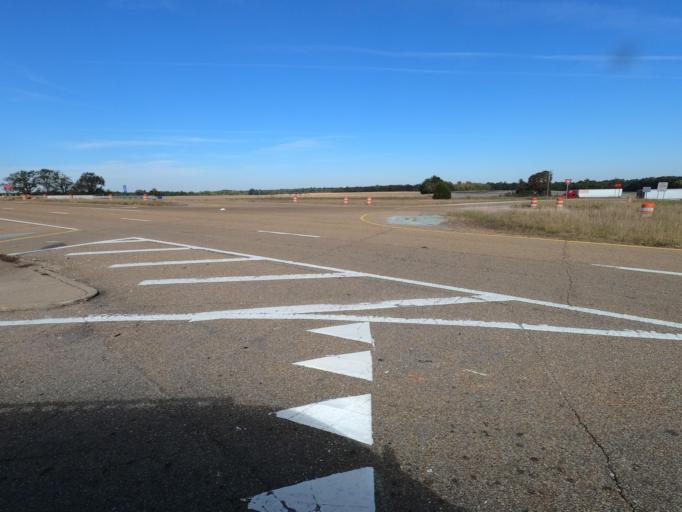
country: US
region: Tennessee
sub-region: Crockett County
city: Bells
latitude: 35.5845
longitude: -89.0919
